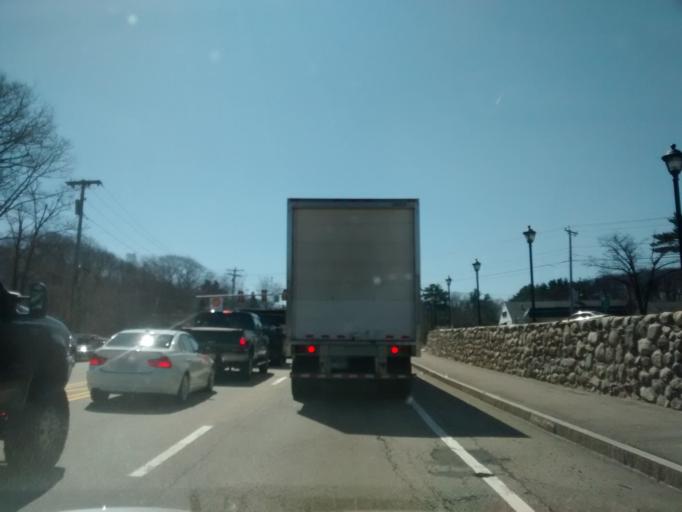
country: US
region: Massachusetts
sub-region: Worcester County
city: Auburn
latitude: 42.1893
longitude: -71.8482
